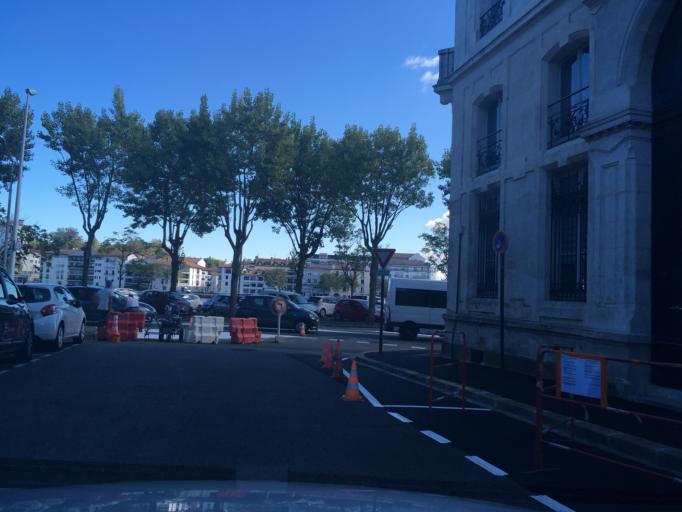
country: FR
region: Aquitaine
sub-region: Departement des Pyrenees-Atlantiques
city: Bayonne
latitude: 43.4917
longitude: -1.4702
